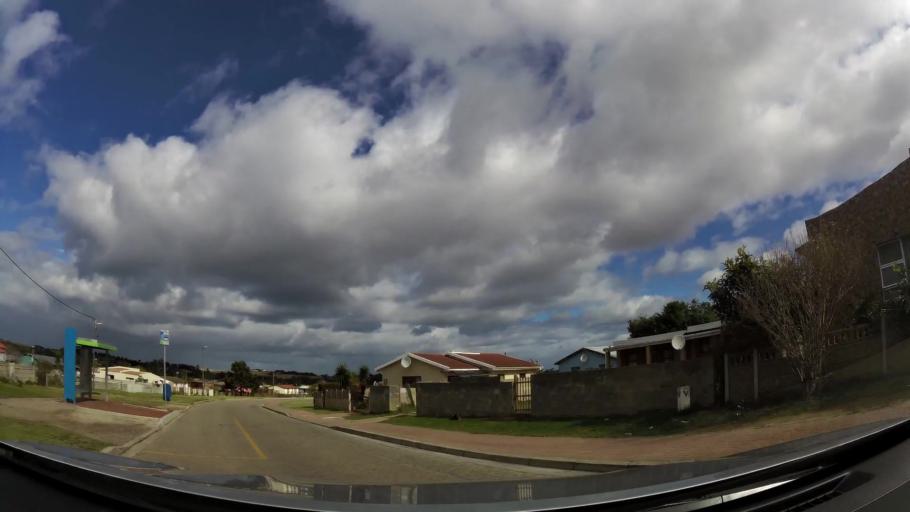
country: ZA
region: Western Cape
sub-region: Eden District Municipality
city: George
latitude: -34.0224
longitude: 22.4703
